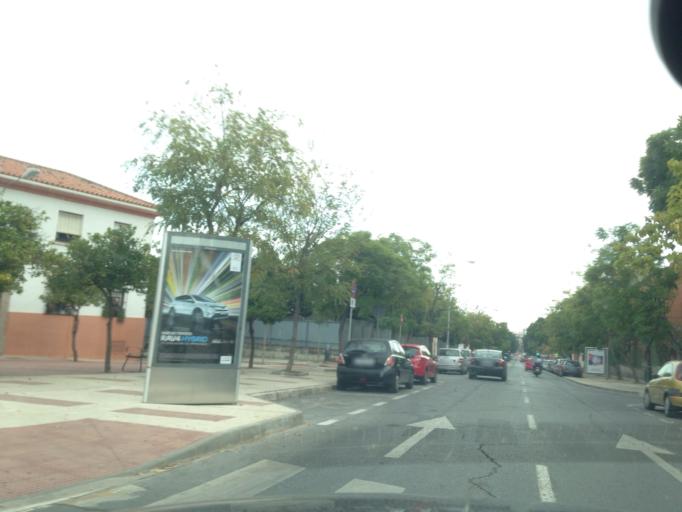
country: ES
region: Andalusia
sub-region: Provincia de Malaga
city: Malaga
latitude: 36.7188
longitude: -4.4466
